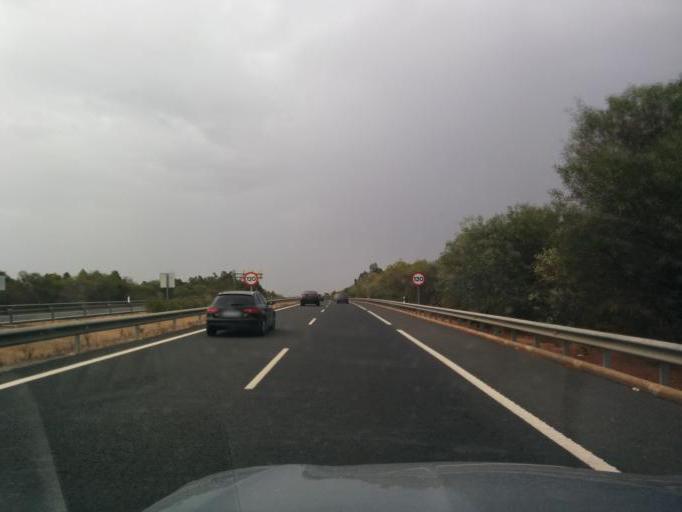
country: ES
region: Andalusia
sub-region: Provincia de Huelva
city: Ayamonte
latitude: 37.2398
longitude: -7.3693
